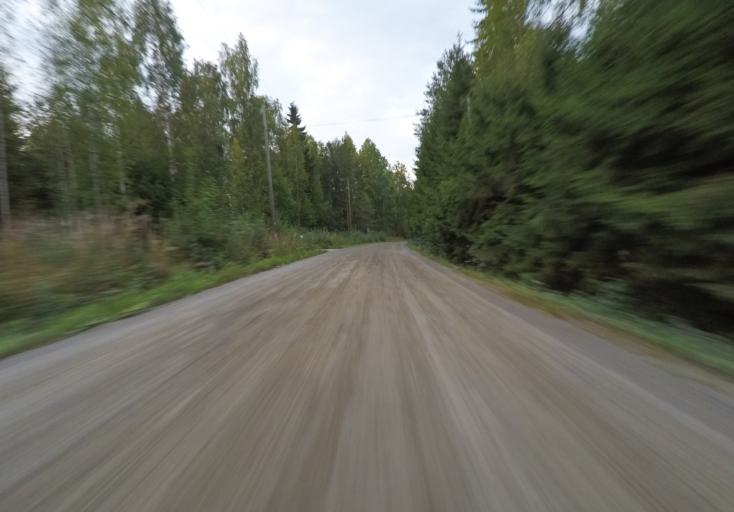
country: FI
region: Central Finland
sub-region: Jyvaeskylae
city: Hankasalmi
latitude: 62.4285
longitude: 26.6452
